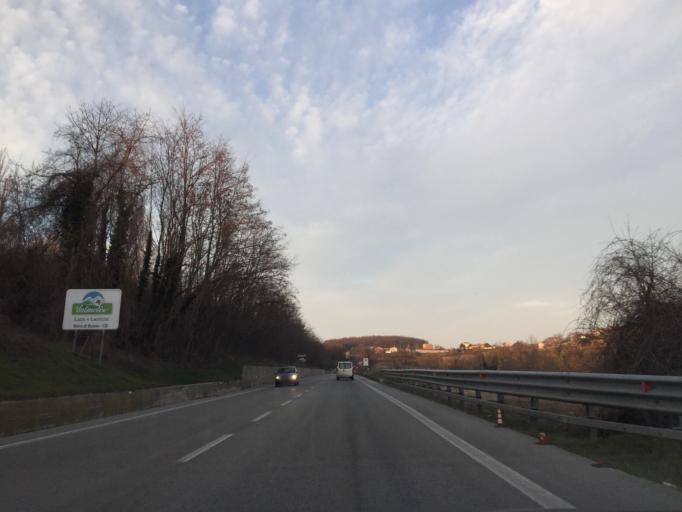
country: IT
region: Molise
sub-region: Provincia di Campobasso
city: Mimosa-Poggio Verde-Nuova Comunita
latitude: 41.5413
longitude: 14.6205
